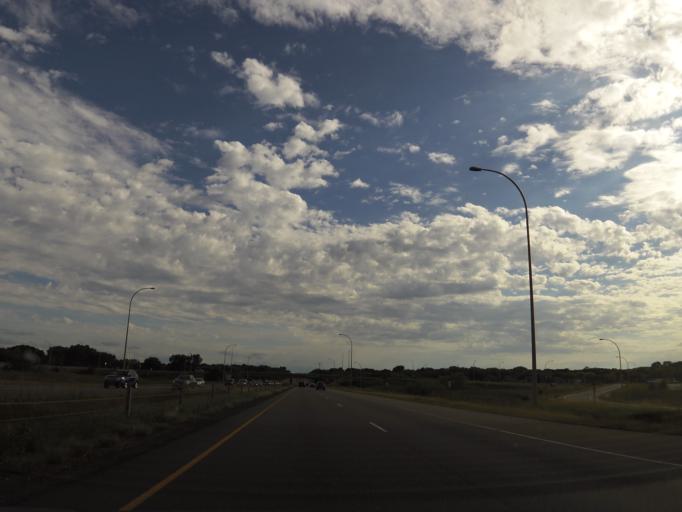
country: US
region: Minnesota
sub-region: Hennepin County
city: New Hope
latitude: 45.0362
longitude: -93.4009
